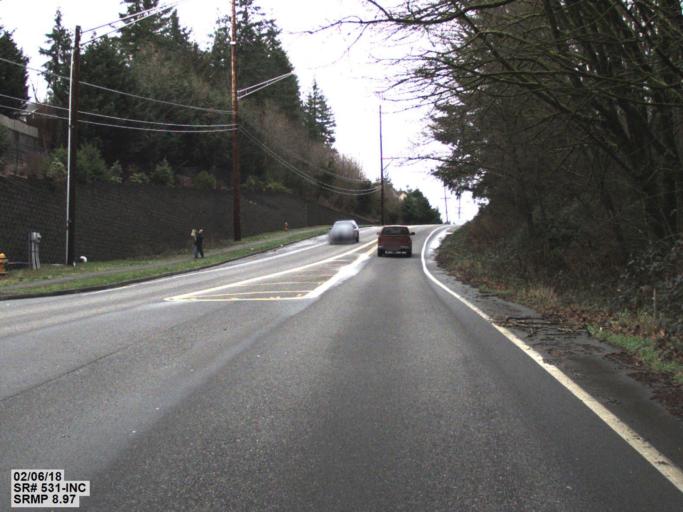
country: US
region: Washington
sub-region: Snohomish County
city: Arlington
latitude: 48.1527
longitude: -122.1327
